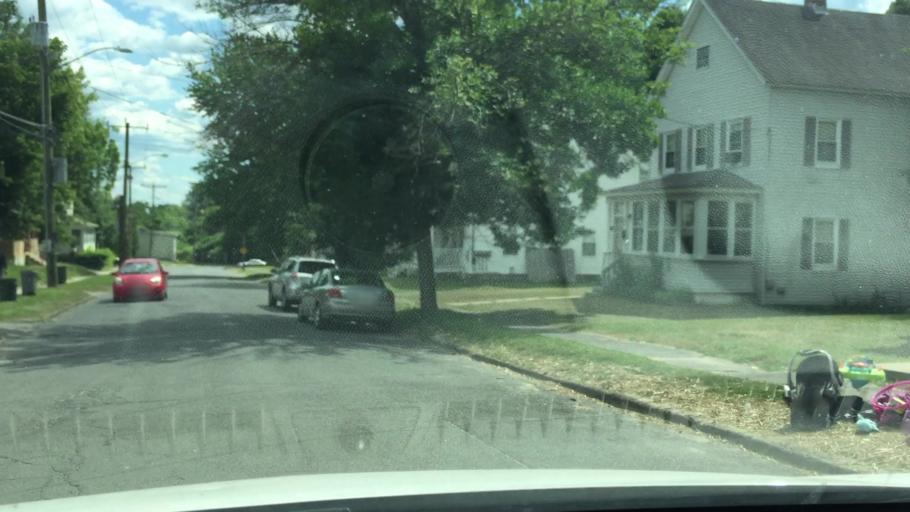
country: US
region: Massachusetts
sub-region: Berkshire County
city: Pittsfield
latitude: 42.4557
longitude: -73.2395
